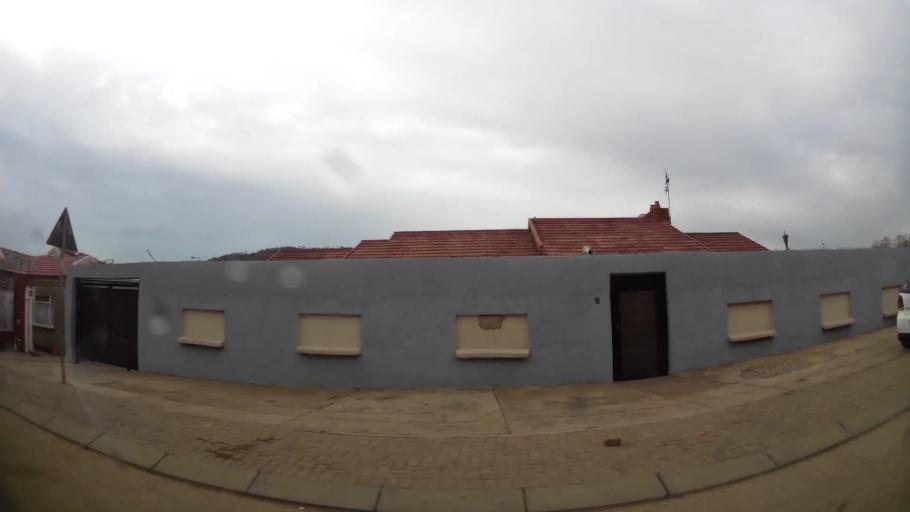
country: ZA
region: Gauteng
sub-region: City of Tshwane Metropolitan Municipality
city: Cullinan
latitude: -25.7048
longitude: 28.3578
